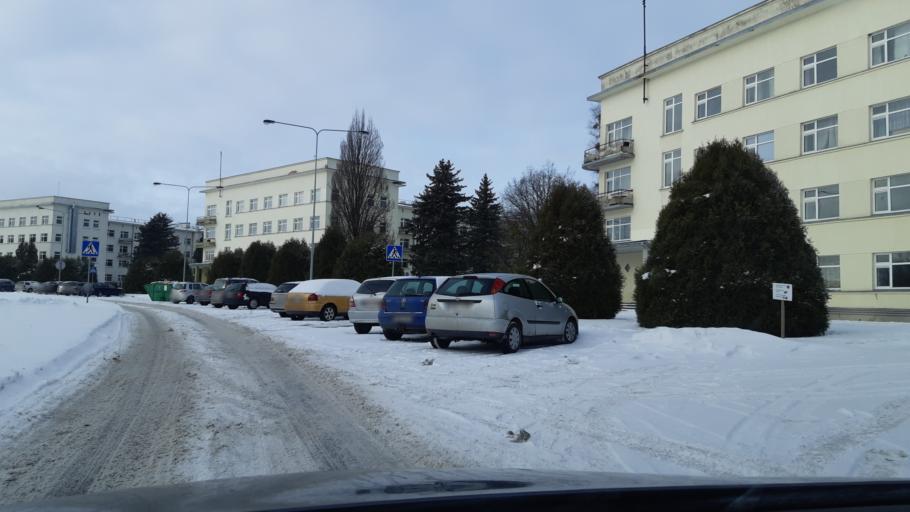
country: LT
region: Kauno apskritis
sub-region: Kauno rajonas
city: Akademija (Kaunas)
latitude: 54.8939
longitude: 23.8334
